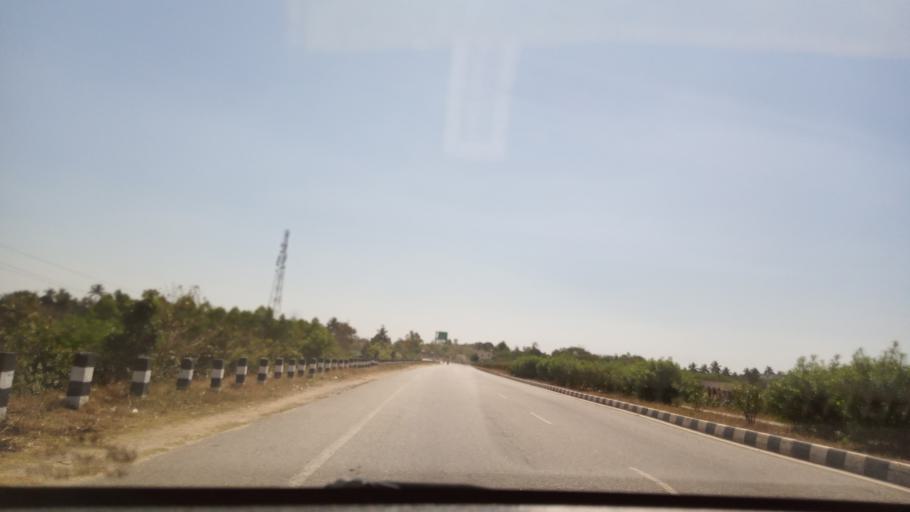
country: IN
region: Karnataka
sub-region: Kolar
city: Mulbagal
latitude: 13.1958
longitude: 78.5338
